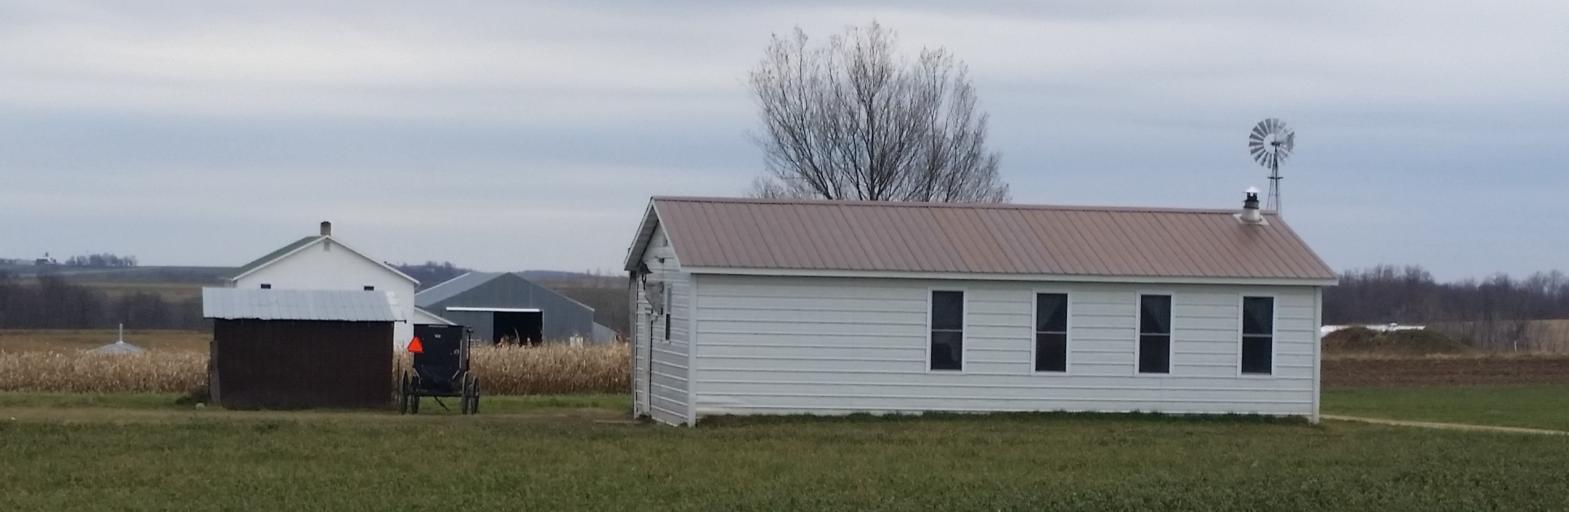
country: US
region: Wisconsin
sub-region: Monroe County
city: Cashton
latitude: 43.7584
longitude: -90.7433
